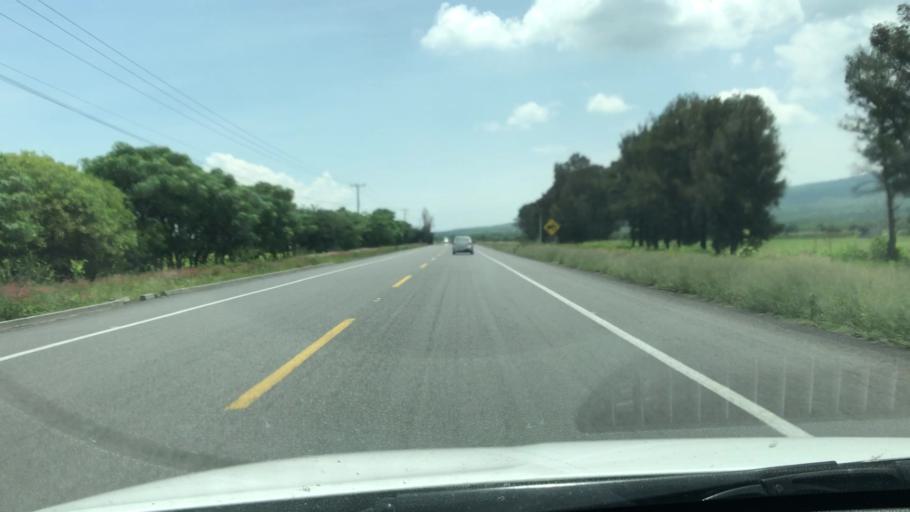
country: MX
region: Michoacan
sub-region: Yurecuaro
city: Yurecuaro
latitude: 20.3410
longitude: -102.1708
